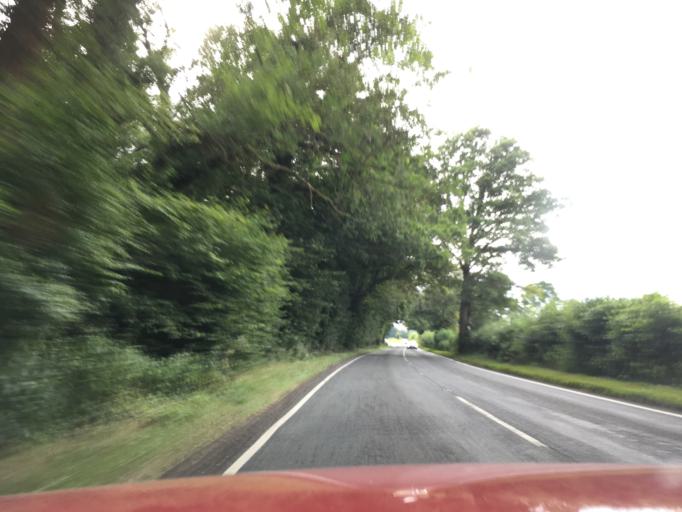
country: GB
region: England
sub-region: Hampshire
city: Four Marks
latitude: 51.0307
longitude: -1.0624
